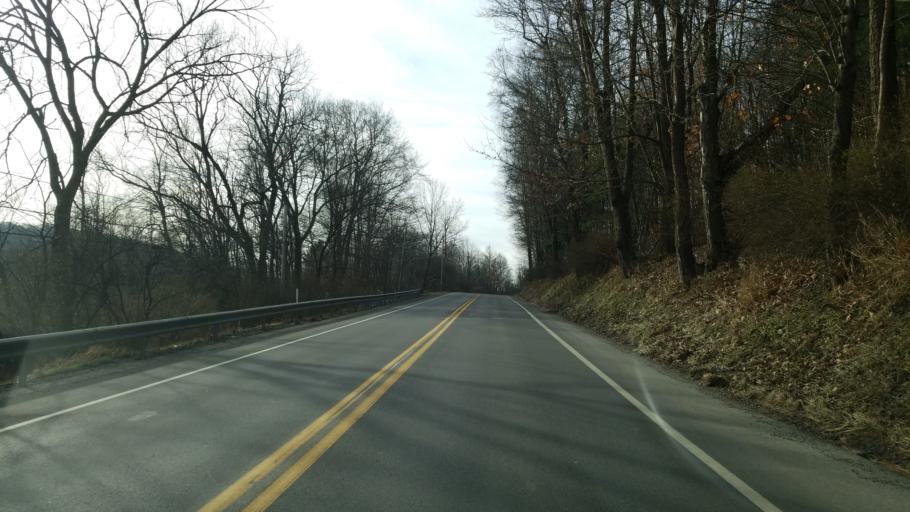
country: US
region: Pennsylvania
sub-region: Jefferson County
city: Albion
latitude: 40.9652
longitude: -78.9098
